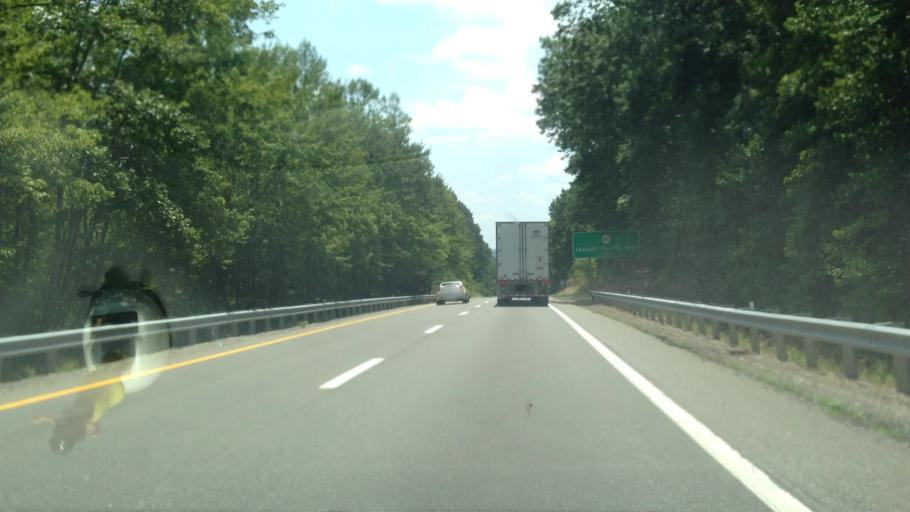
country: US
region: Virginia
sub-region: City of Martinsville
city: Martinsville
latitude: 36.6379
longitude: -79.8936
